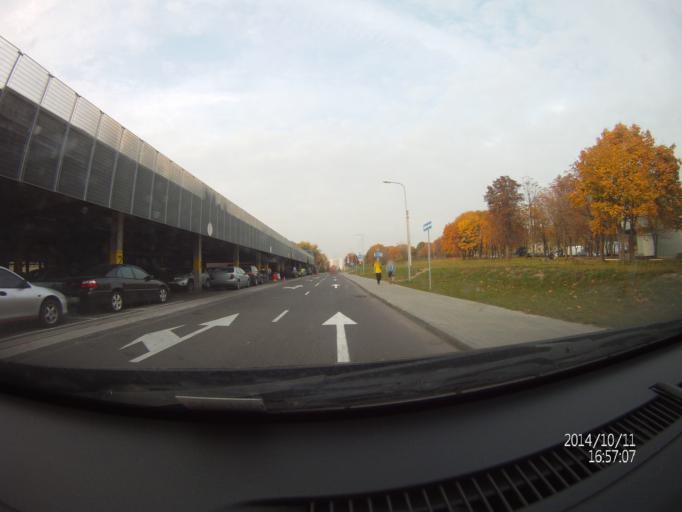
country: BY
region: Minsk
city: Novoye Medvezhino
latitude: 53.9086
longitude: 27.4715
